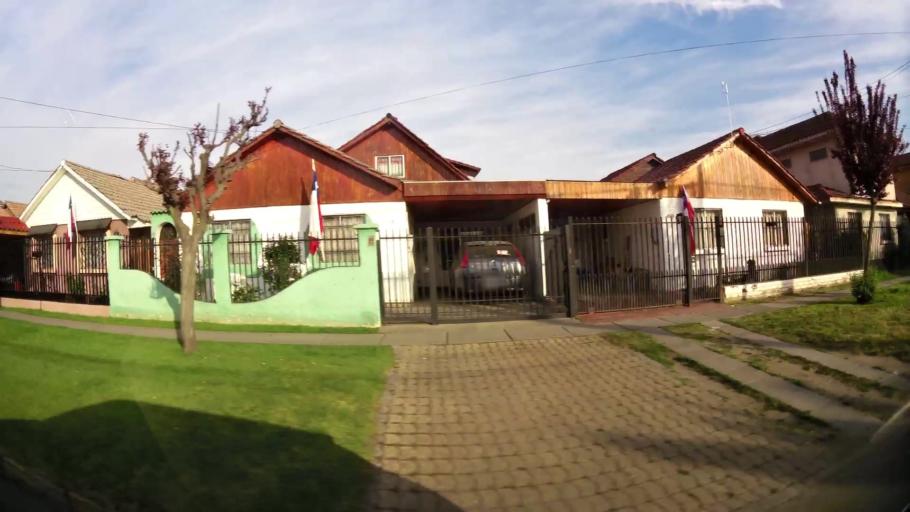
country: CL
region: Santiago Metropolitan
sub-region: Provincia de Maipo
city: San Bernardo
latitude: -33.5598
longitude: -70.7850
